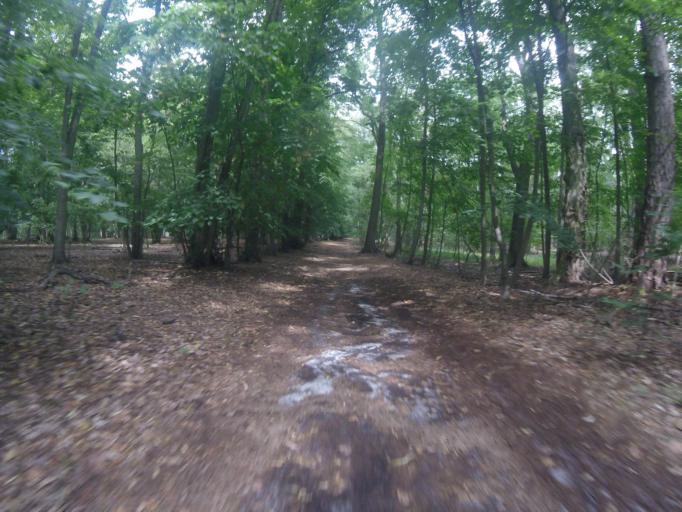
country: DE
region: Brandenburg
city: Konigs Wusterhausen
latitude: 52.2774
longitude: 13.6113
